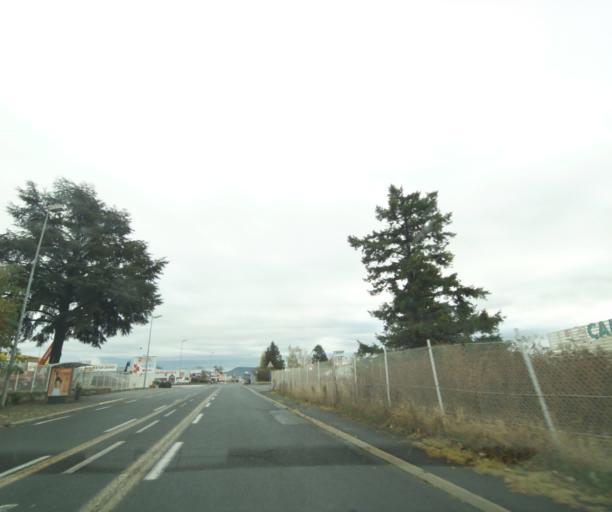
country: FR
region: Auvergne
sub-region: Departement du Puy-de-Dome
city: Perignat-les-Sarlieve
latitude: 45.7470
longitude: 3.1627
